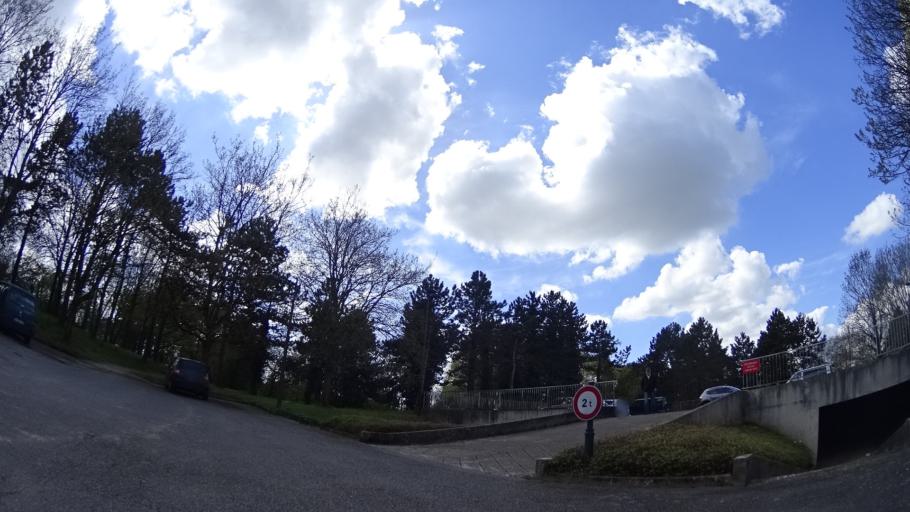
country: FR
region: Brittany
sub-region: Departement d'Ille-et-Vilaine
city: Rennes
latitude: 48.1329
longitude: -1.6663
